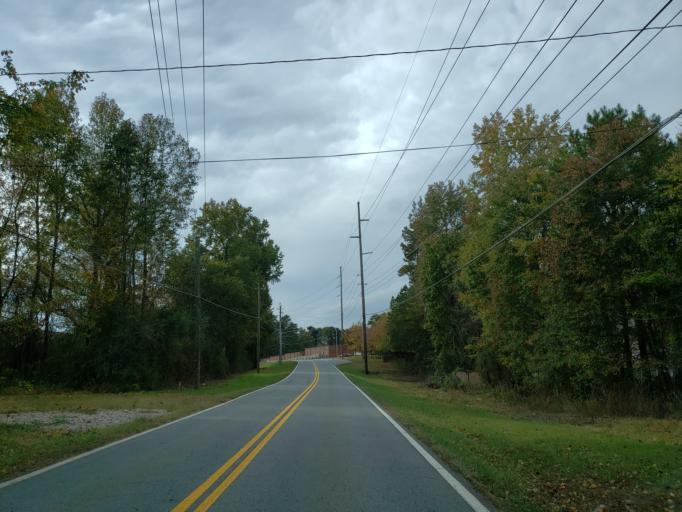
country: US
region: Georgia
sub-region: Cobb County
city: Acworth
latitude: 34.0633
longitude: -84.6481
